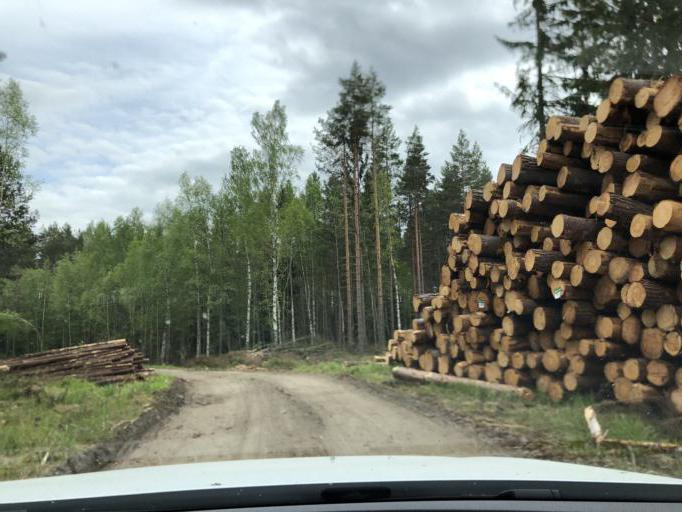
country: SE
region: Uppsala
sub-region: Heby Kommun
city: OEstervala
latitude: 60.3742
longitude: 17.2322
